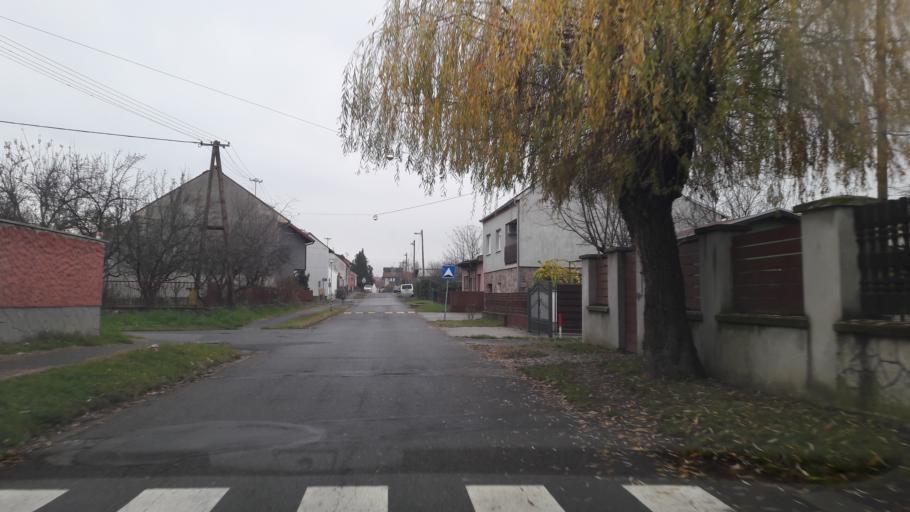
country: HR
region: Osjecko-Baranjska
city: Visnjevac
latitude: 45.5644
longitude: 18.6156
